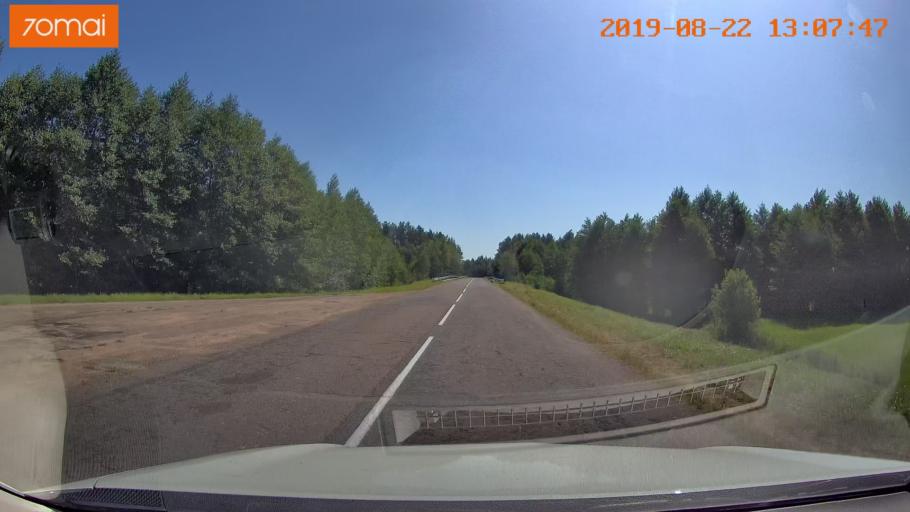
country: BY
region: Minsk
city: Prawdzinski
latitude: 53.3321
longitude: 27.8389
